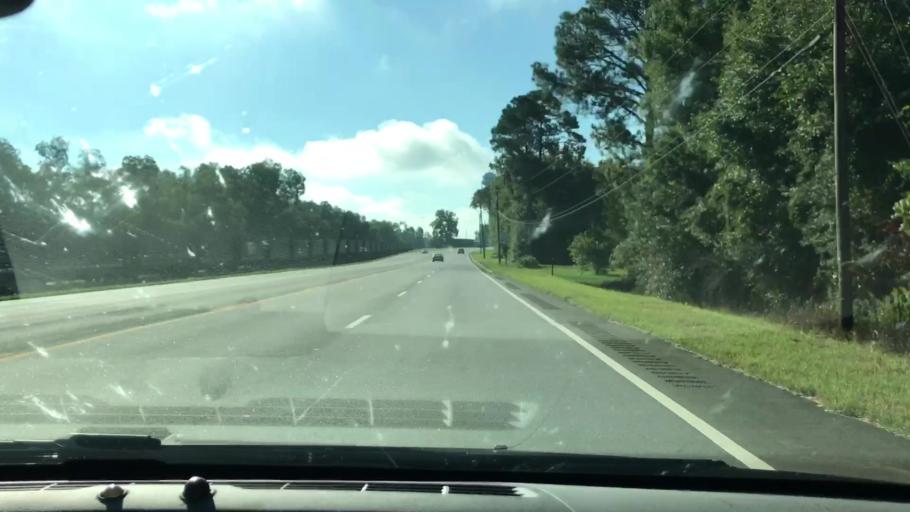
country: US
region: Georgia
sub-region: Terrell County
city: Dawson
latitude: 31.7230
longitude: -84.3528
